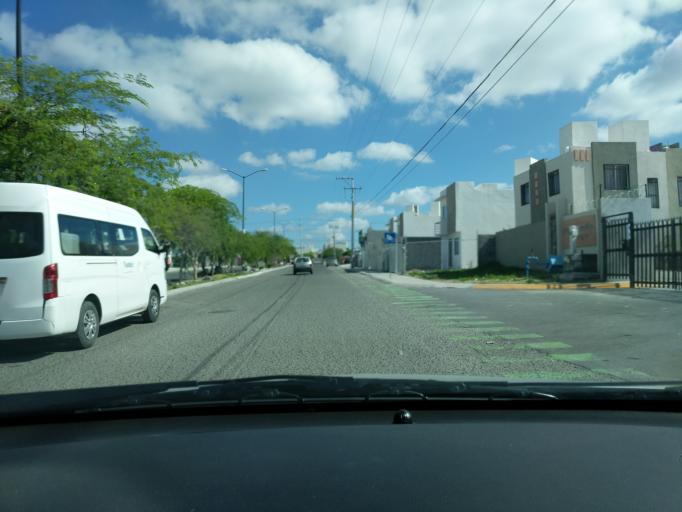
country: MX
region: Queretaro
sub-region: Queretaro
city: Patria Nueva
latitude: 20.6397
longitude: -100.4827
